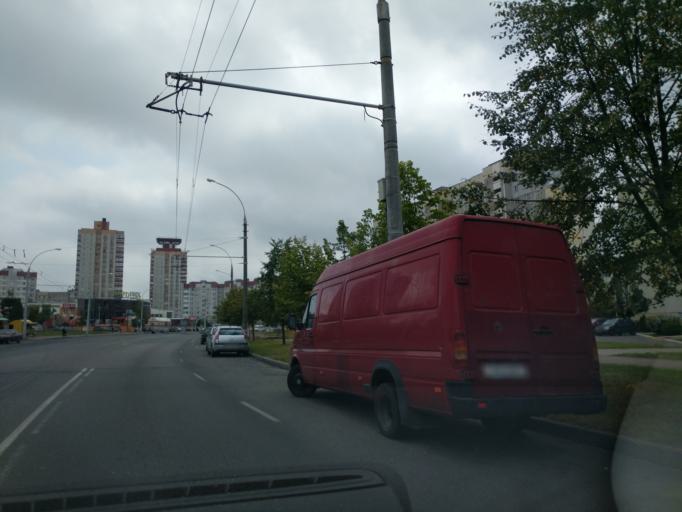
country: BY
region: Minsk
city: Novoye Medvezhino
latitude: 53.8866
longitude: 27.4351
